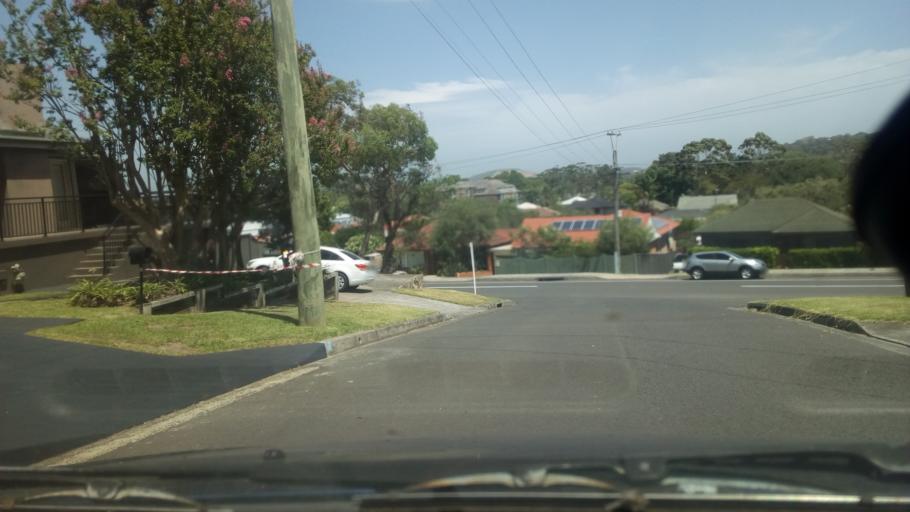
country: AU
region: New South Wales
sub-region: Wollongong
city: West Wollongong
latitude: -34.4311
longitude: 150.8649
